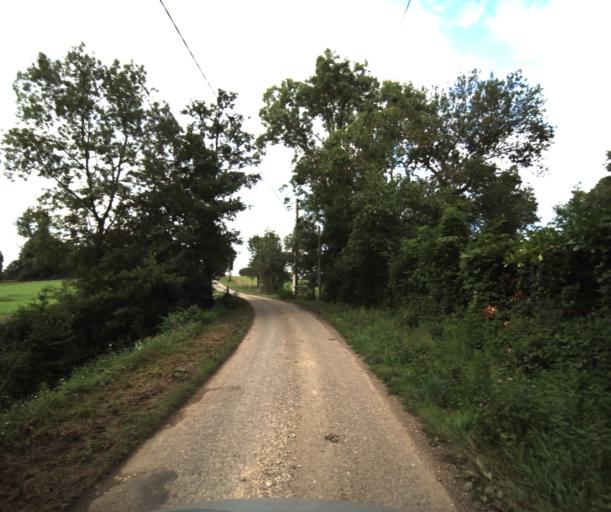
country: FR
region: Midi-Pyrenees
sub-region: Departement de la Haute-Garonne
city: Lacasse
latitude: 43.3900
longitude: 1.2385
